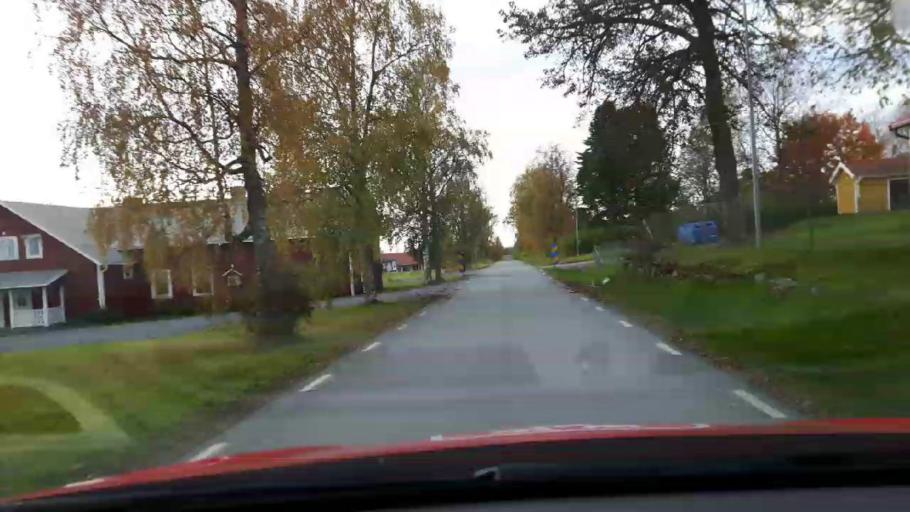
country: SE
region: Jaemtland
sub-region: Krokoms Kommun
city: Krokom
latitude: 63.3673
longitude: 14.4838
